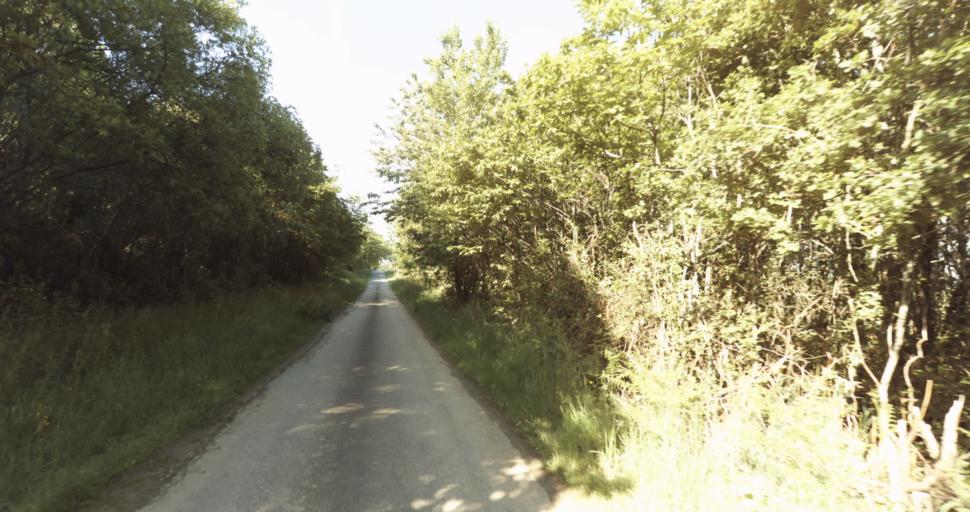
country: FR
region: Limousin
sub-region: Departement de la Haute-Vienne
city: Bosmie-l'Aiguille
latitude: 45.7196
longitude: 1.2305
